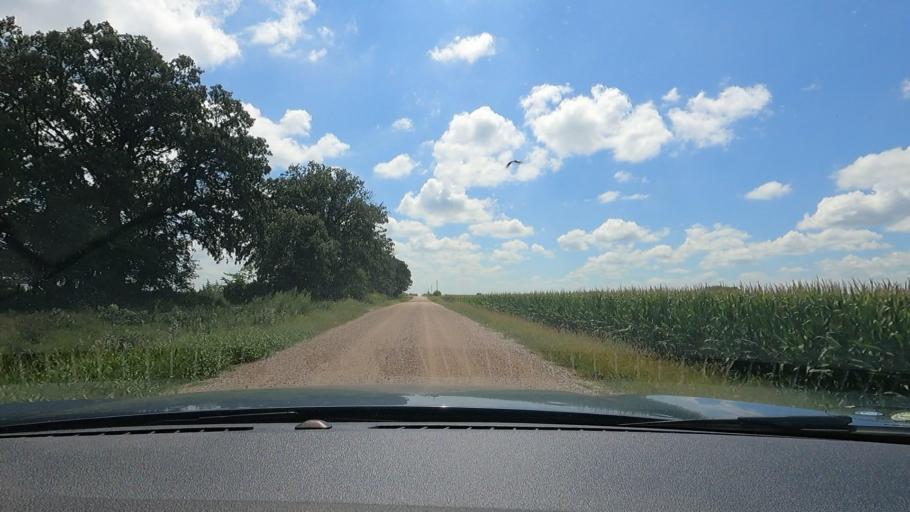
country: US
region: Nebraska
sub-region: Saunders County
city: Wahoo
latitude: 41.2657
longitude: -96.5418
